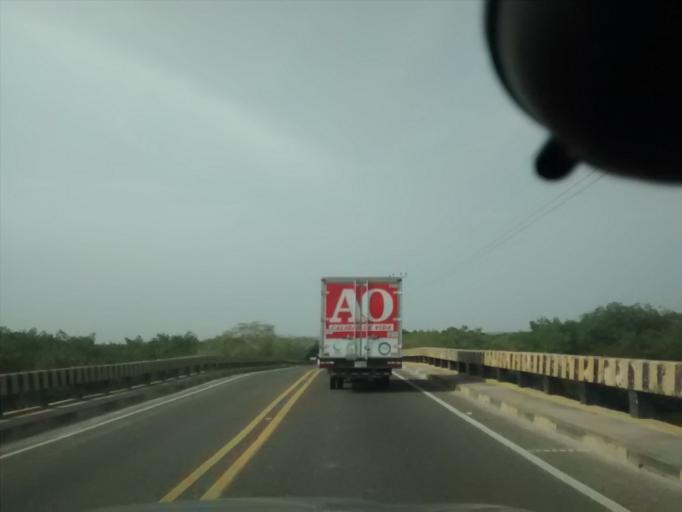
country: CO
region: Bolivar
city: Cartagena
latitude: 10.4844
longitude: -75.4863
